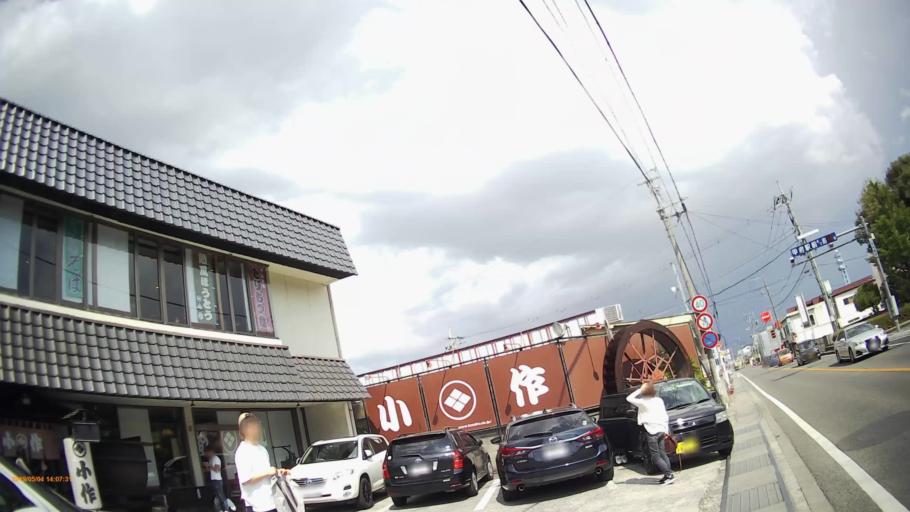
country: JP
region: Yamanashi
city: Kofu-shi
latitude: 35.6611
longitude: 138.5401
